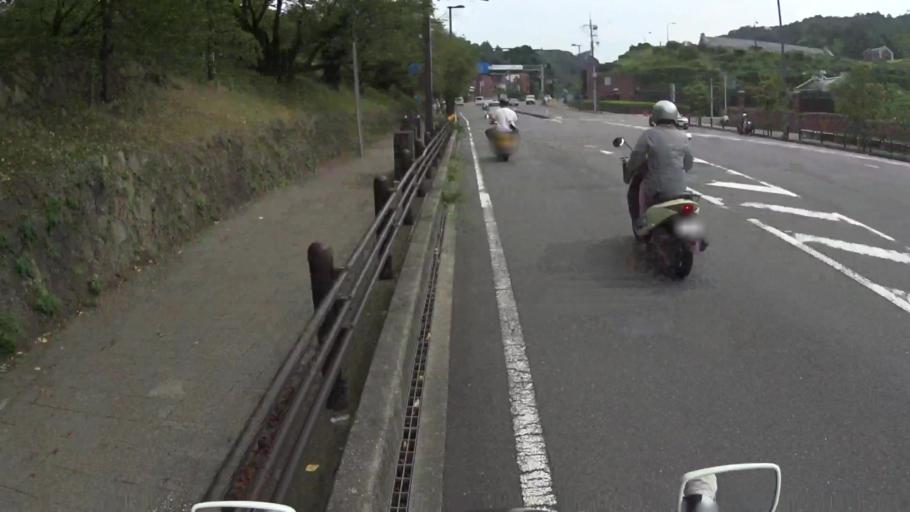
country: JP
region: Kyoto
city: Kyoto
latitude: 35.0090
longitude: 135.7896
